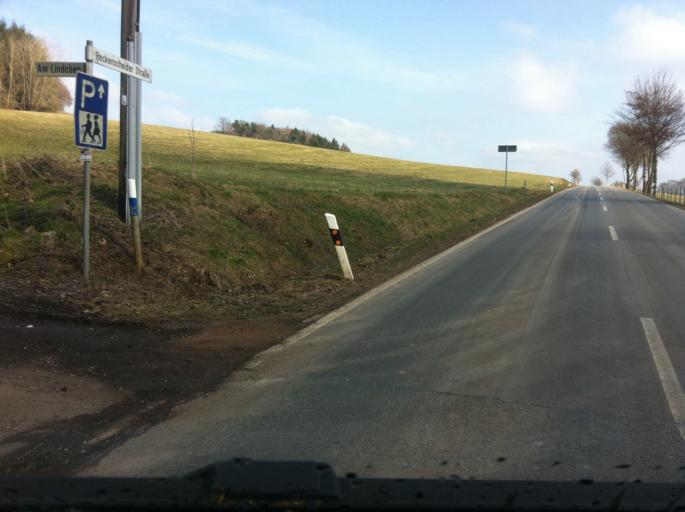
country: DE
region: Rheinland-Pfalz
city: Hummel
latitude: 50.5089
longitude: 6.8239
